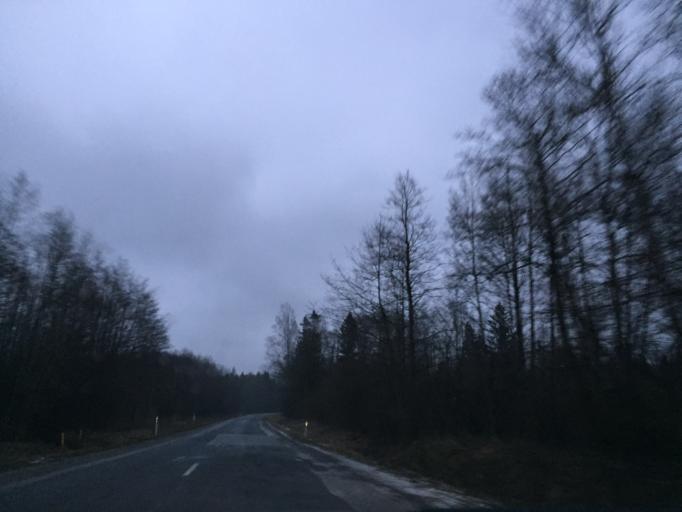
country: EE
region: Saare
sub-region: Kuressaare linn
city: Kuressaare
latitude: 58.5787
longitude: 22.6318
